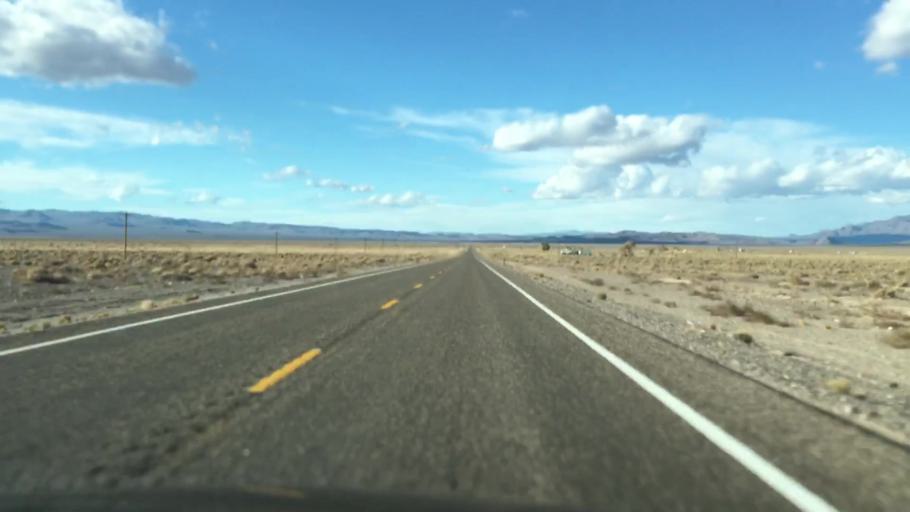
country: US
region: Nevada
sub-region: Nye County
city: Beatty
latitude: 37.2457
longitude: -116.9993
